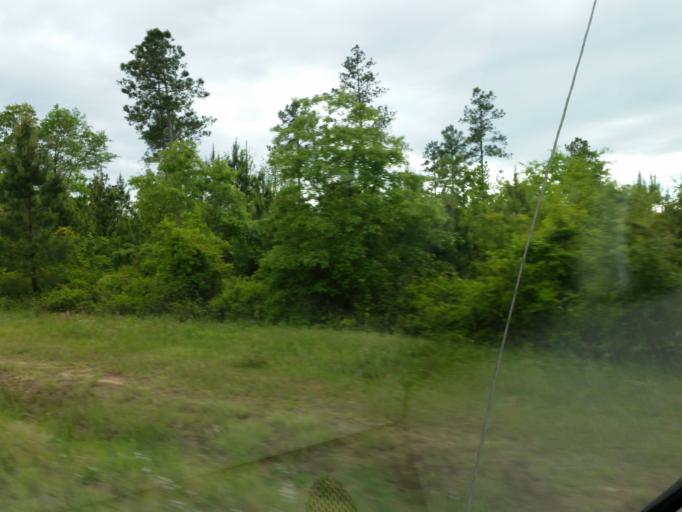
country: US
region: Georgia
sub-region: Crawford County
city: Knoxville
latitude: 32.7147
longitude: -83.9484
